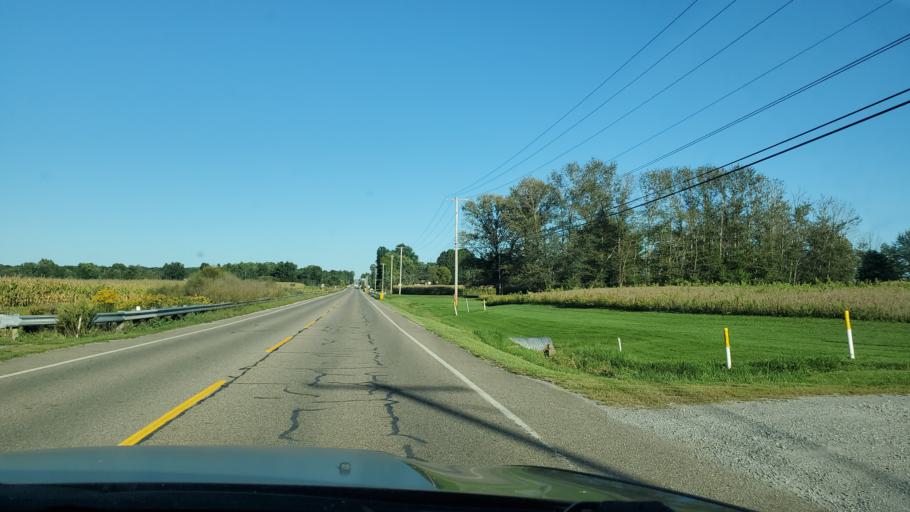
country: US
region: Ohio
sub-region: Mahoning County
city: Canfield
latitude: 40.9882
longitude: -80.7722
